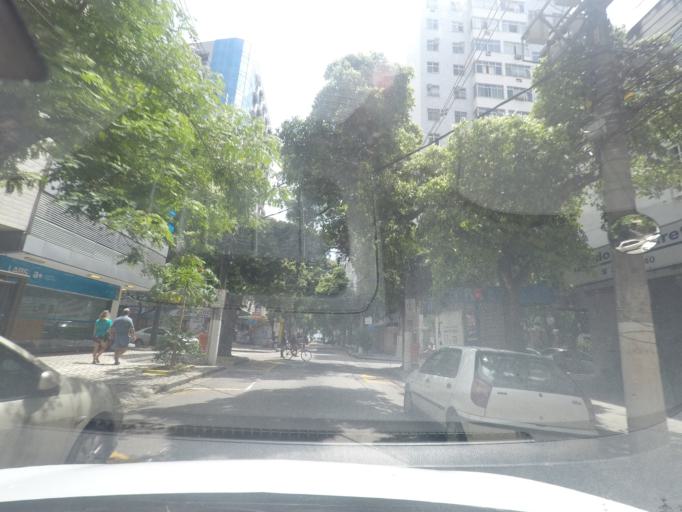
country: BR
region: Rio de Janeiro
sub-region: Niteroi
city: Niteroi
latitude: -22.9060
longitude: -43.1092
